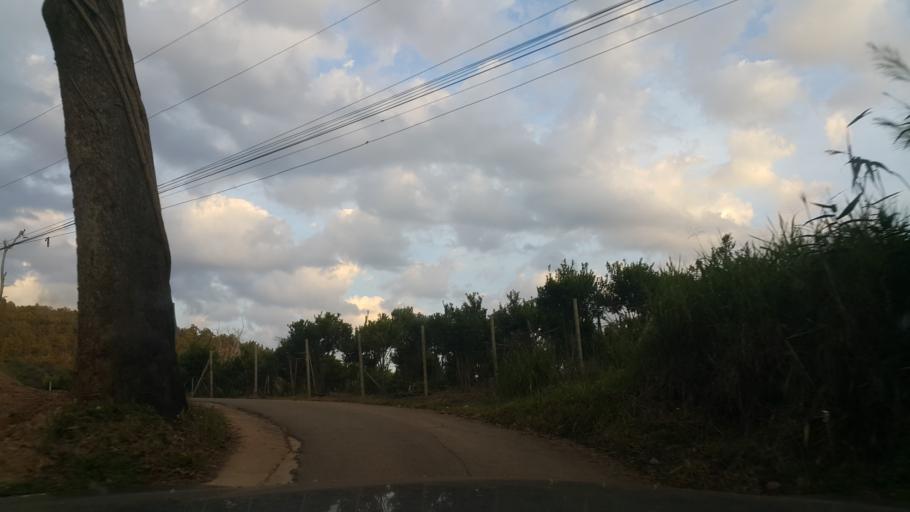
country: TH
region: Chiang Mai
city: Samoeng
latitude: 18.9738
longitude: 98.6805
